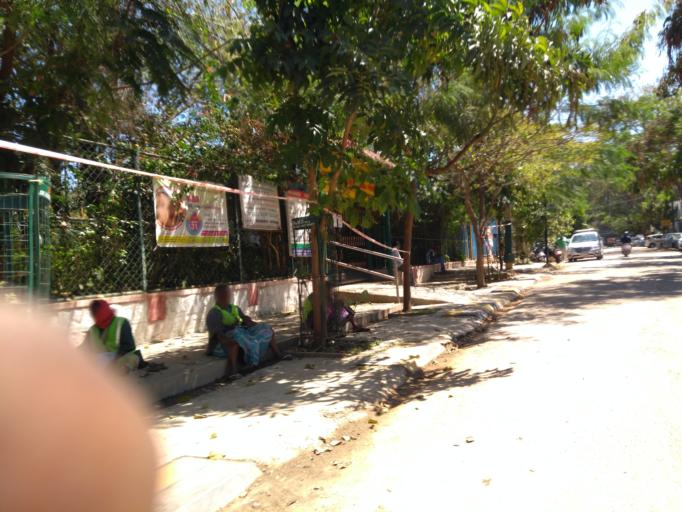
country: IN
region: Karnataka
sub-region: Bangalore Urban
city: Bangalore
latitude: 12.9695
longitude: 77.6530
